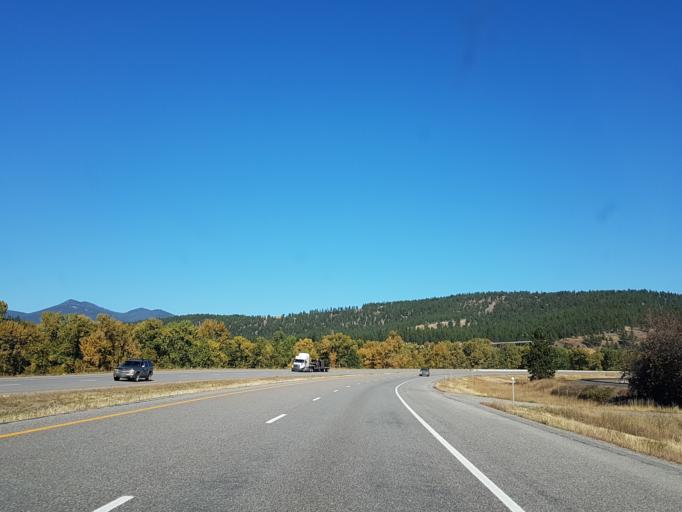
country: US
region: Montana
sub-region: Missoula County
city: Frenchtown
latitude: 47.0220
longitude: -114.3942
